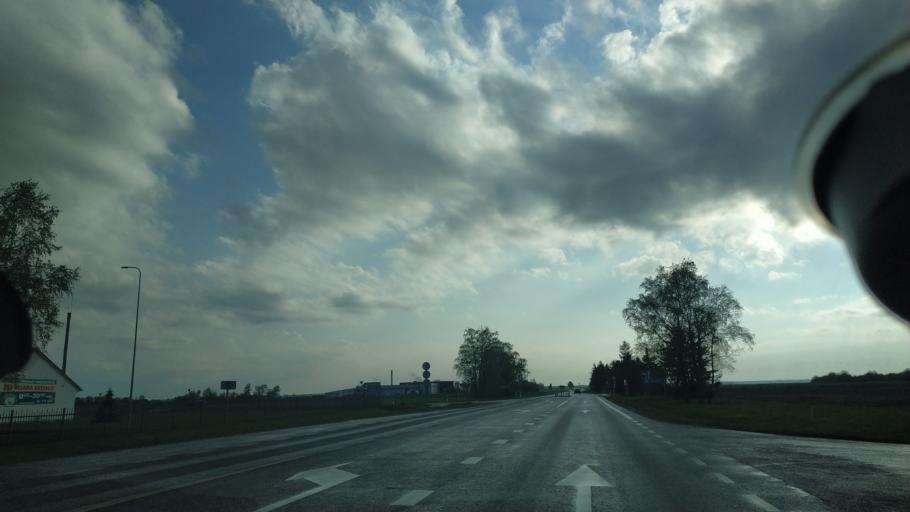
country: LT
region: Kauno apskritis
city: Kedainiai
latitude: 55.2640
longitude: 23.8990
